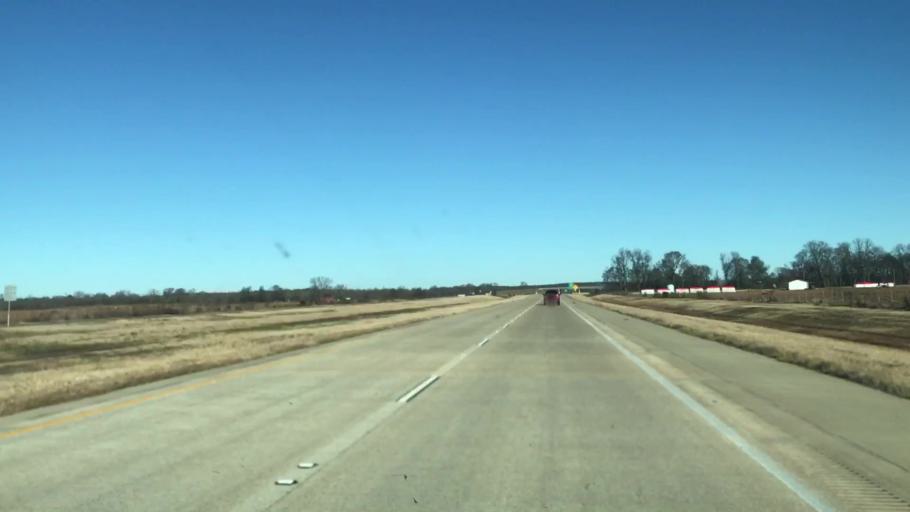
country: US
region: Louisiana
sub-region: Caddo Parish
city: Oil City
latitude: 32.7568
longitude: -93.8843
